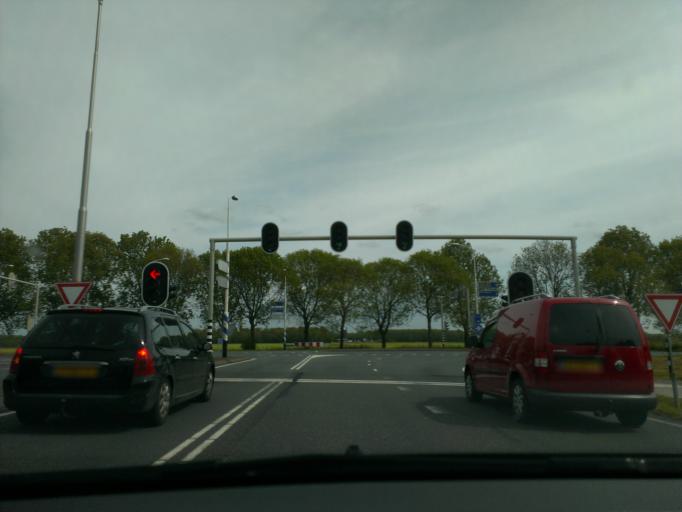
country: NL
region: Gelderland
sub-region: Gemeente Harderwijk
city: Harderwijk
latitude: 52.4062
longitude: 5.5926
